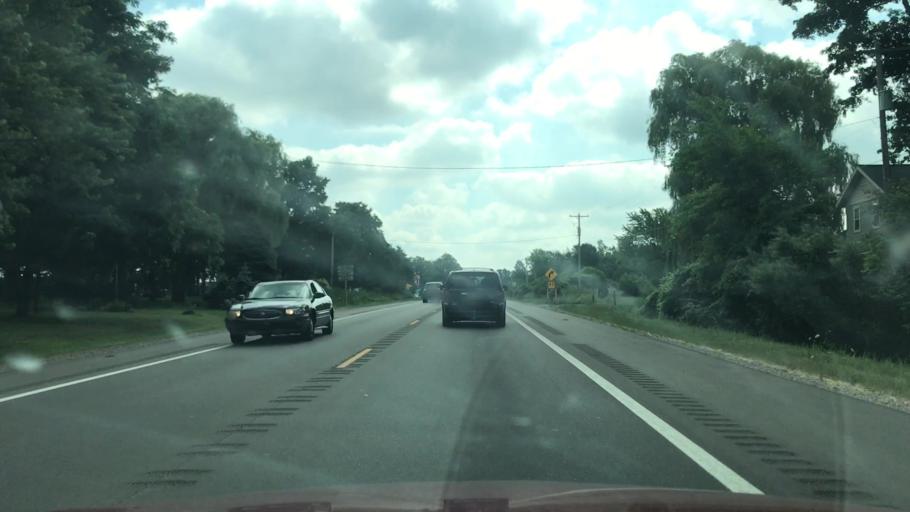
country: US
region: Michigan
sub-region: Kent County
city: Kent City
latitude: 43.2344
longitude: -85.8043
